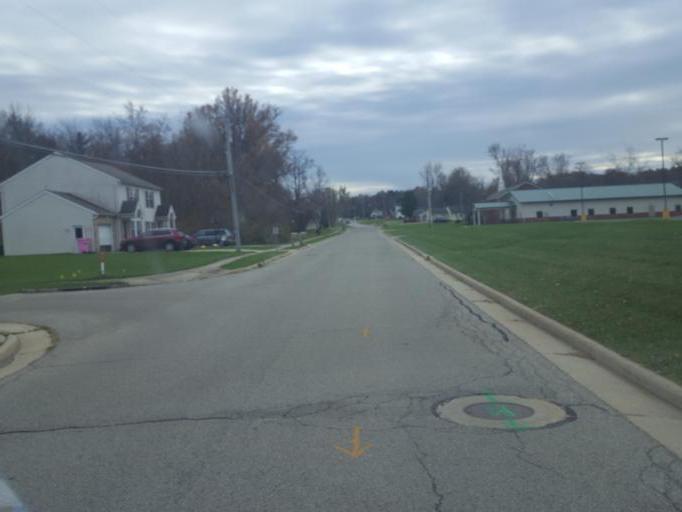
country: US
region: Ohio
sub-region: Richland County
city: Ontario
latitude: 40.7615
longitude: -82.5825
